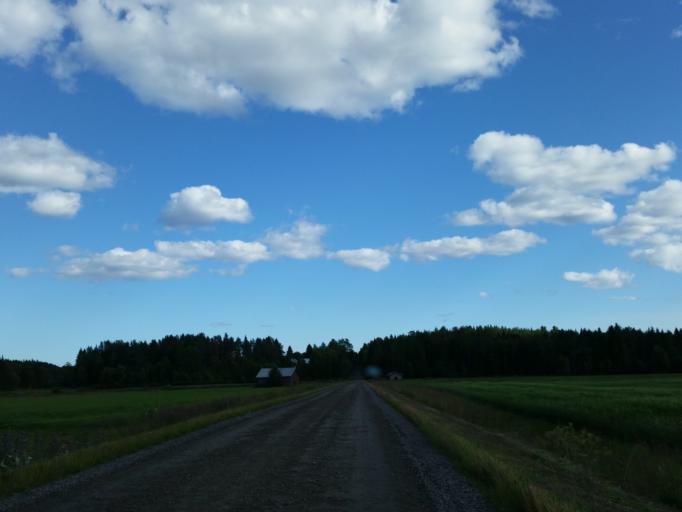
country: SE
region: Vaesterbotten
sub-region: Robertsfors Kommun
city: Robertsfors
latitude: 64.1274
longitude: 20.8896
